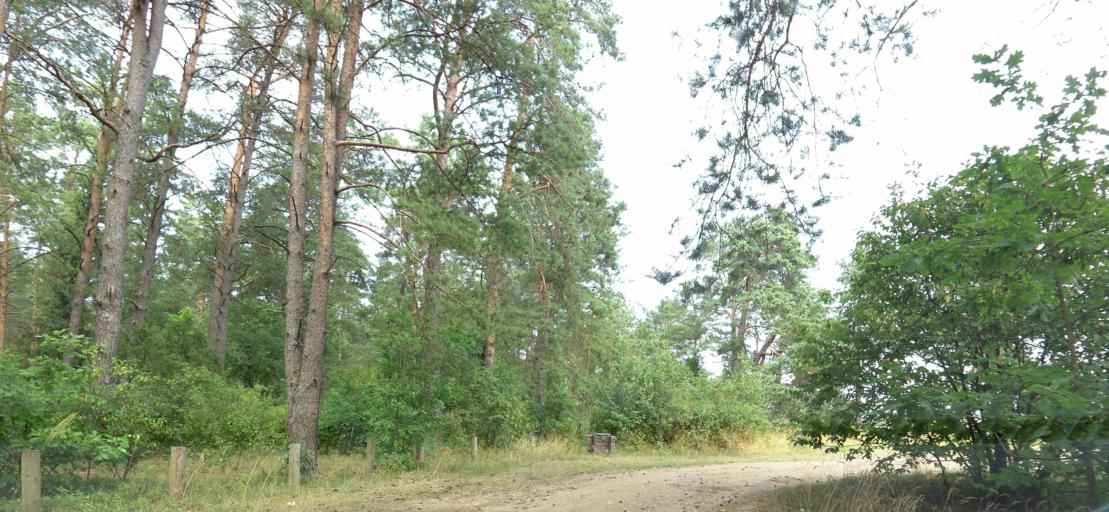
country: LT
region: Vilnius County
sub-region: Trakai
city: Rudiskes
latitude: 54.3520
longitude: 24.8405
